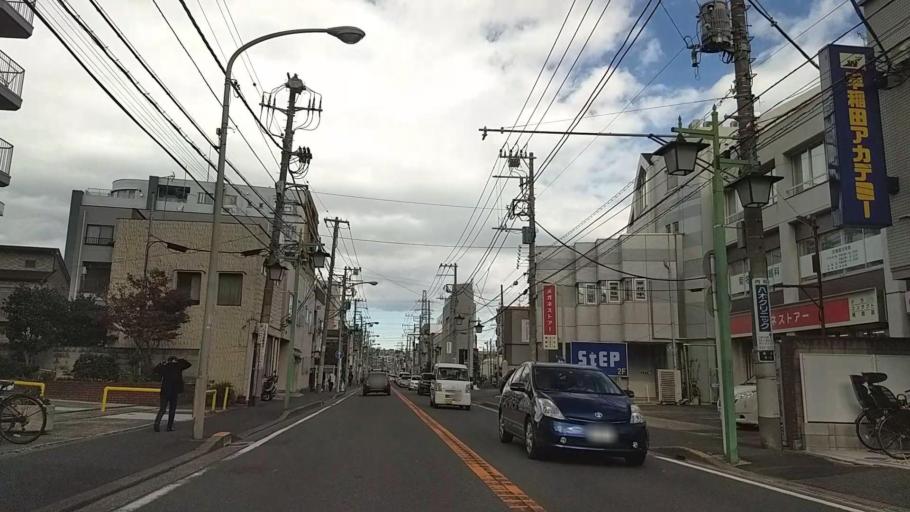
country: JP
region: Kanagawa
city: Yokohama
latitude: 35.5121
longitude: 139.6318
